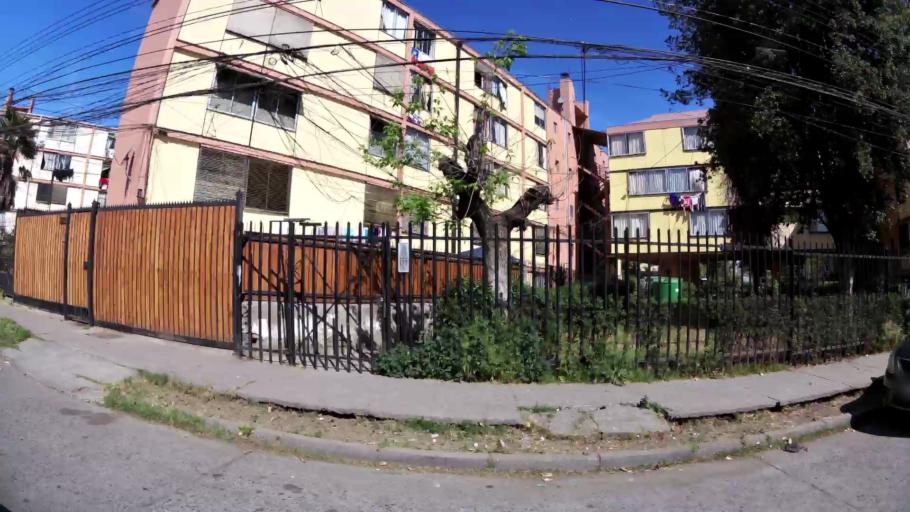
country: CL
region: Santiago Metropolitan
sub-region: Provincia de Santiago
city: Santiago
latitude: -33.4264
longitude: -70.6644
